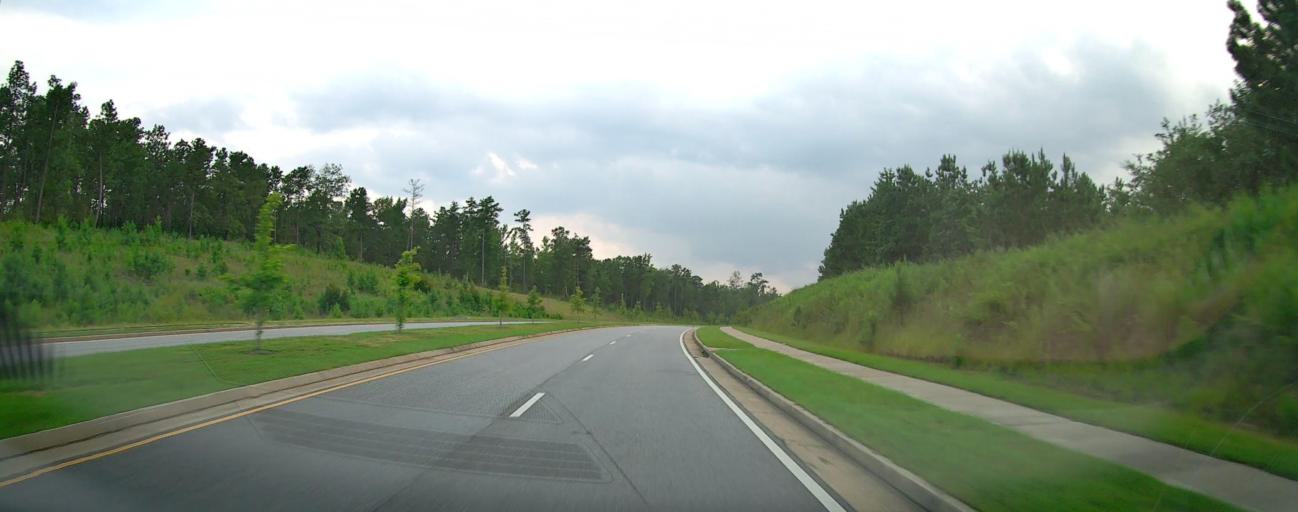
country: US
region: Georgia
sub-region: Muscogee County
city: Columbus
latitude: 32.5138
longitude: -84.8468
